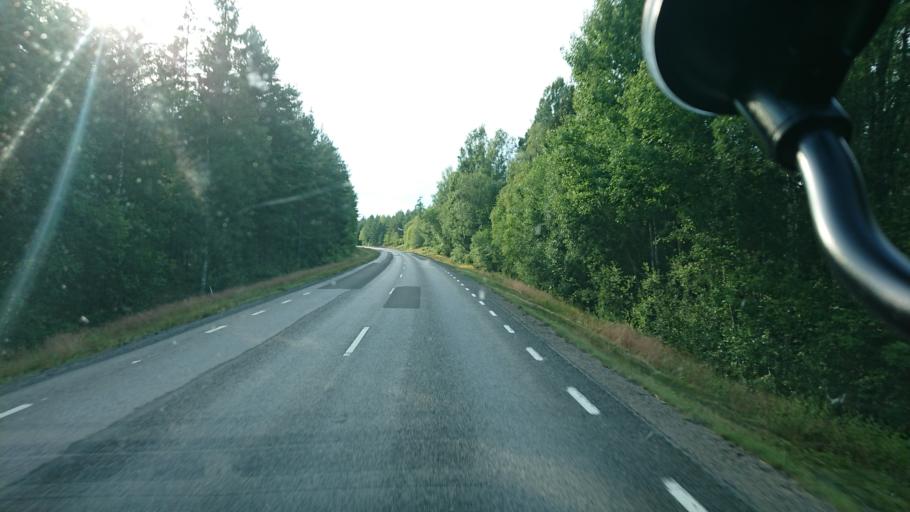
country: SE
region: Kronoberg
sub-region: Vaxjo Kommun
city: Rottne
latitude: 57.0300
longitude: 14.9732
